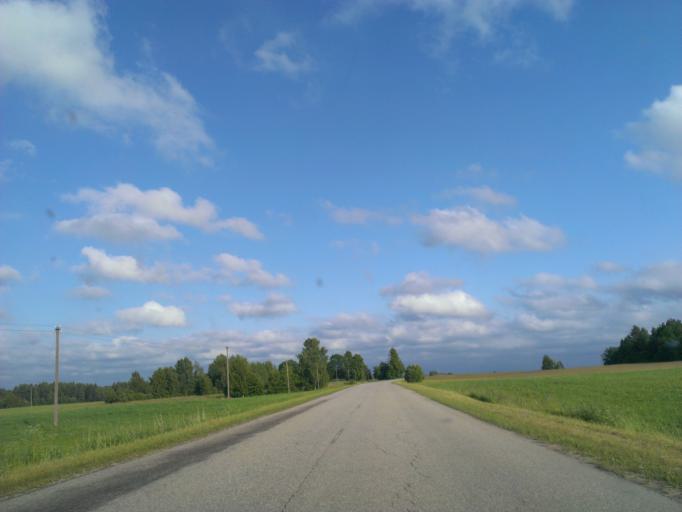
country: LV
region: Aizpute
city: Aizpute
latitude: 56.7723
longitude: 21.5262
